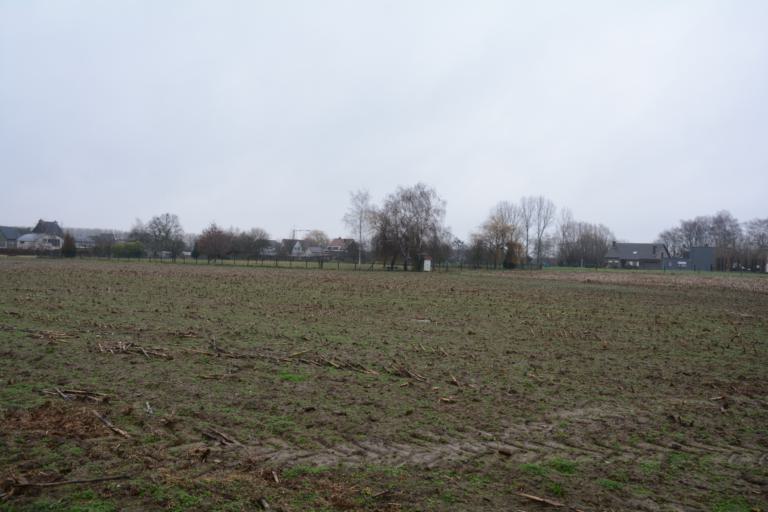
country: BE
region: Flanders
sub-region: Provincie Oost-Vlaanderen
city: Lebbeke
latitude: 50.9595
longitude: 4.1315
